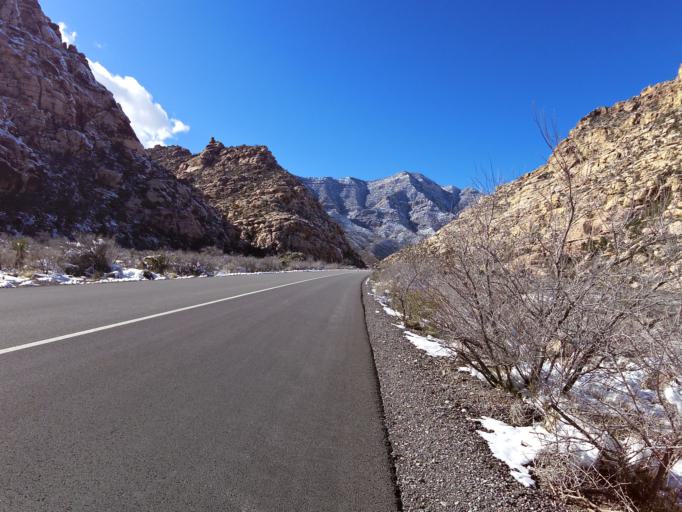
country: US
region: Nevada
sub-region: Clark County
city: Summerlin South
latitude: 36.1584
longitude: -115.4957
